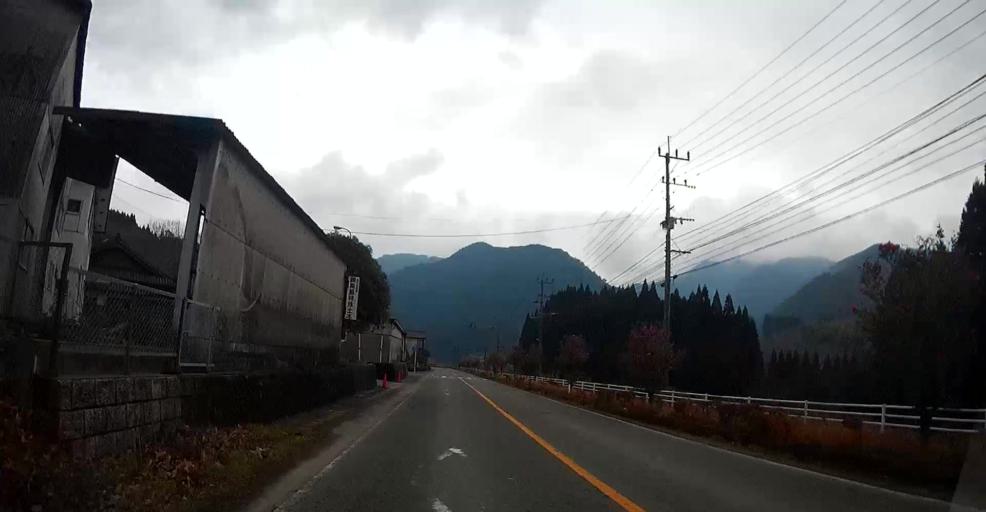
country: JP
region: Kumamoto
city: Matsubase
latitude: 32.6180
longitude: 130.8368
